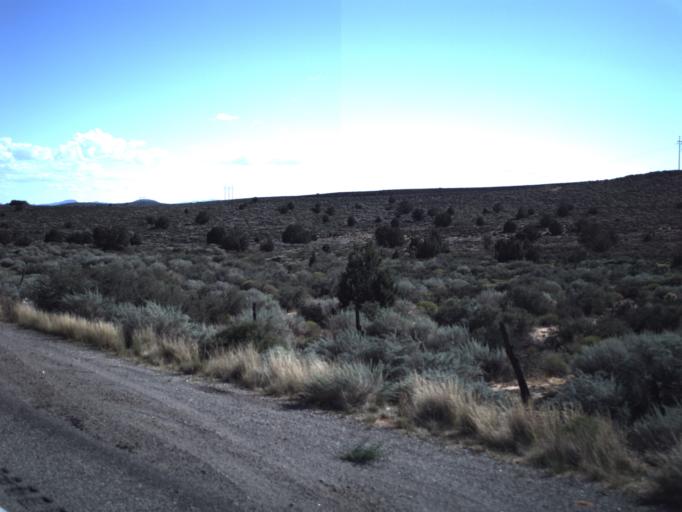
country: US
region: Utah
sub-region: Washington County
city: Toquerville
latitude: 37.2654
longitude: -113.2955
